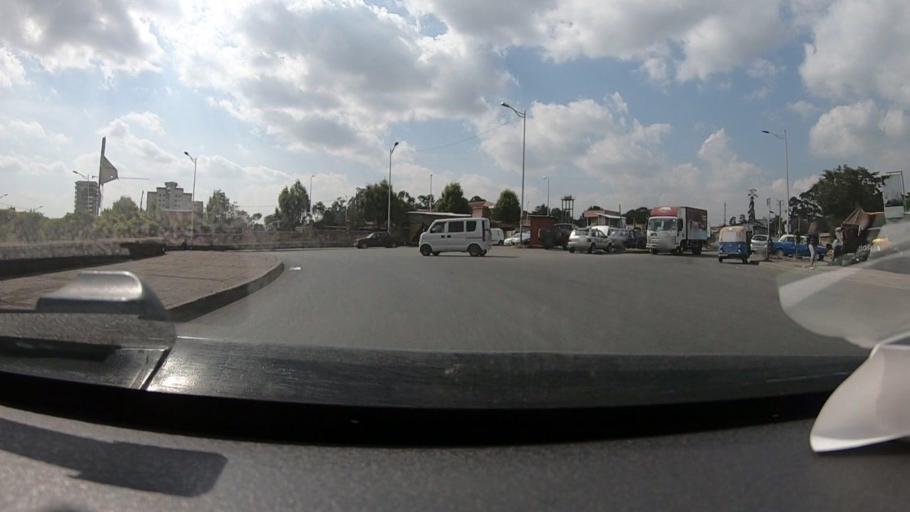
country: ET
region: Adis Abeba
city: Addis Ababa
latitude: 9.0468
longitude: 38.7683
